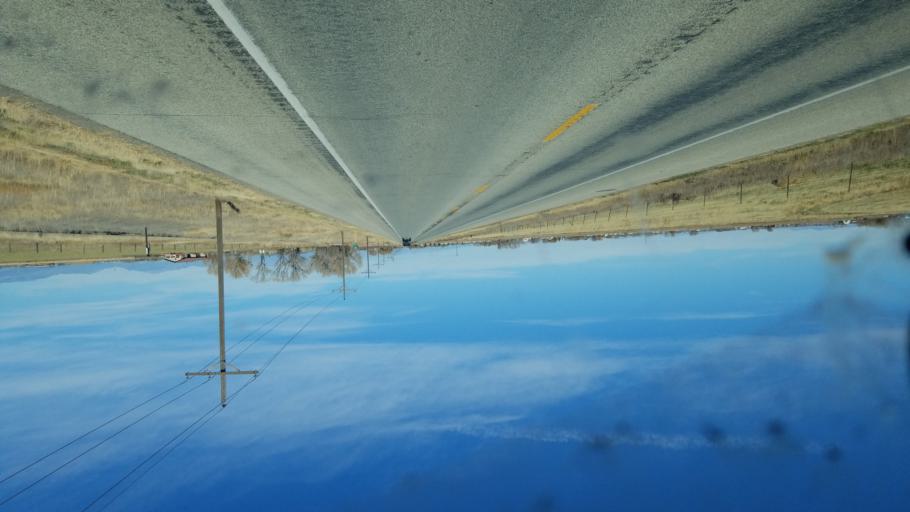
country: US
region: Colorado
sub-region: Conejos County
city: Conejos
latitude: 37.2059
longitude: -105.9793
